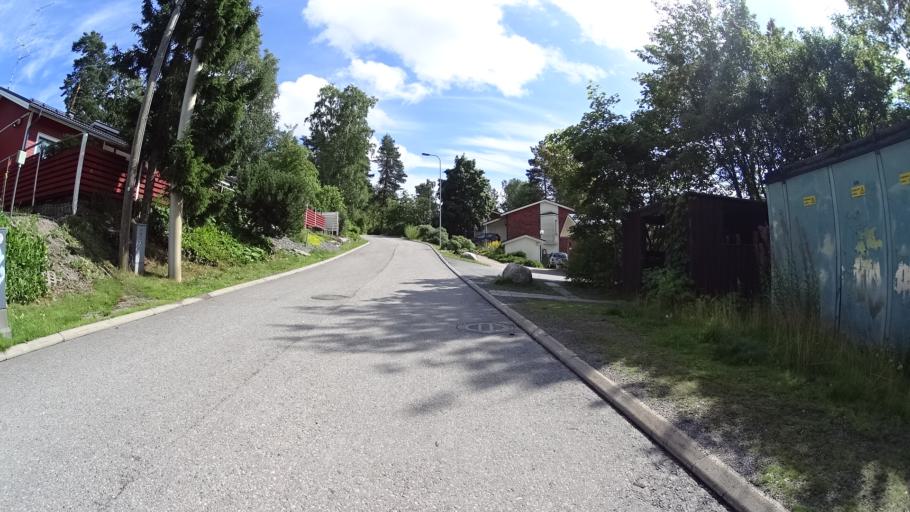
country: FI
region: Uusimaa
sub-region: Helsinki
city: Kilo
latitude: 60.2020
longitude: 24.7674
